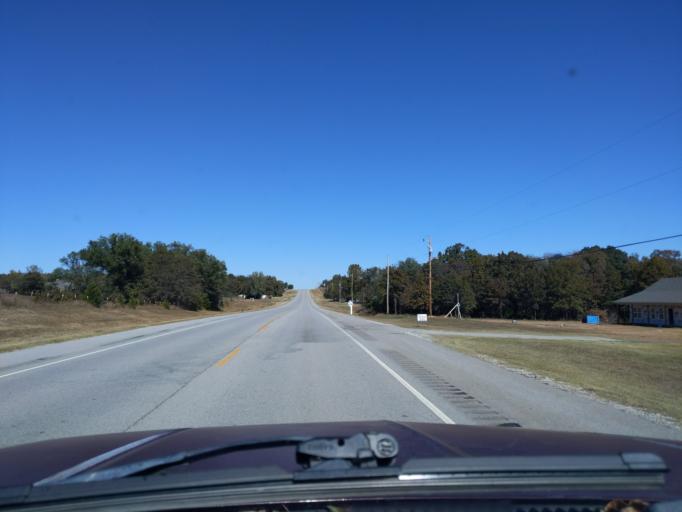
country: US
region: Oklahoma
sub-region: Creek County
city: Bristow
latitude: 35.7636
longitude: -96.3872
